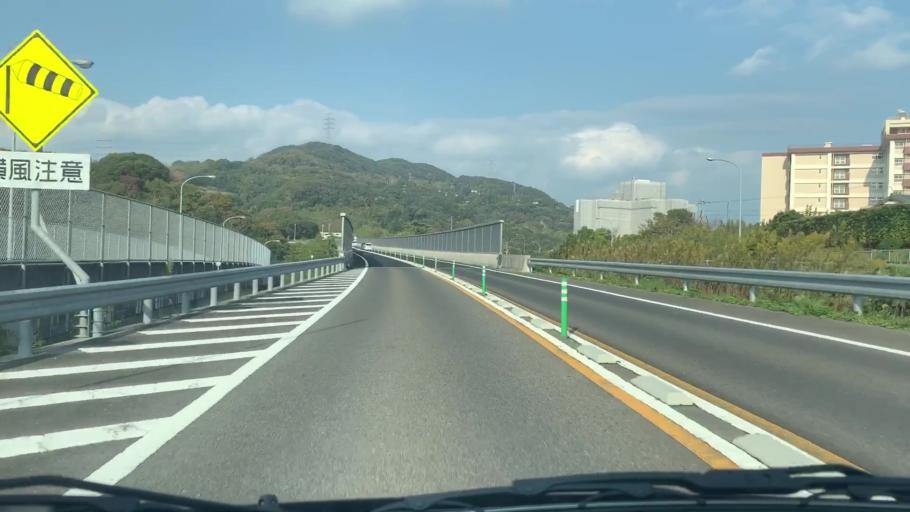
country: JP
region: Nagasaki
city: Sasebo
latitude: 33.0821
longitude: 129.7761
